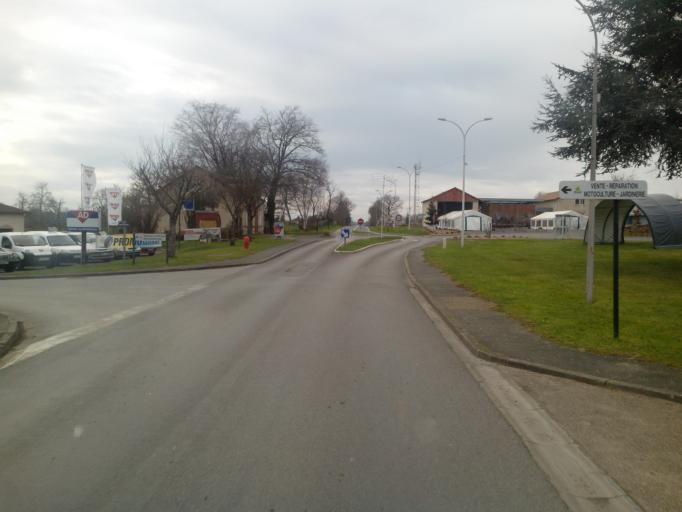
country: FR
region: Limousin
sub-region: Departement de la Haute-Vienne
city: Magnac-Laval
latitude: 46.2154
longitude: 1.1615
